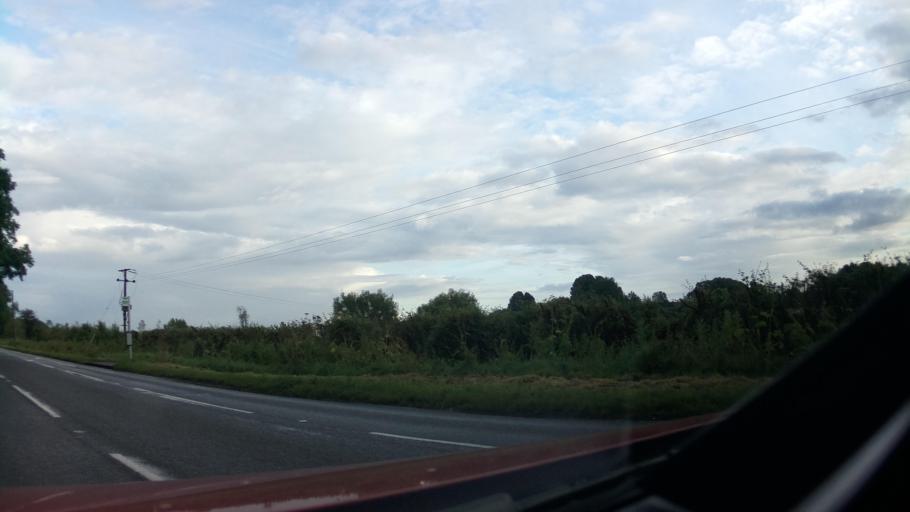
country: GB
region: England
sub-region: Oxfordshire
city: Kidlington
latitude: 51.8372
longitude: -1.3069
